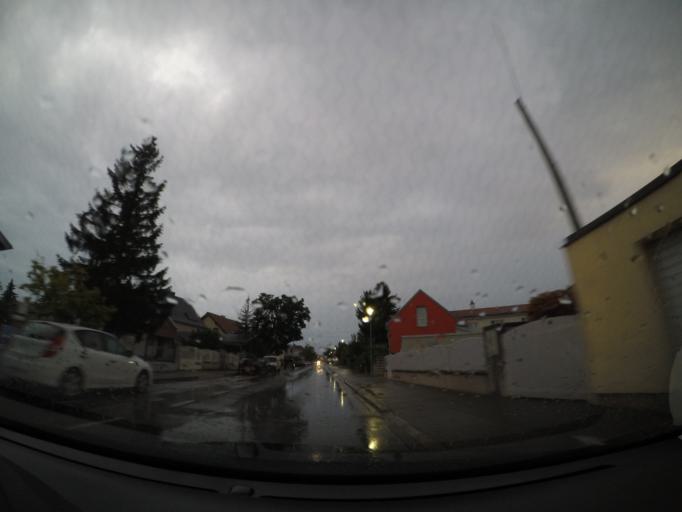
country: AT
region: Lower Austria
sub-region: Politischer Bezirk Baden
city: Bad Voslau
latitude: 47.9603
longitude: 16.2123
